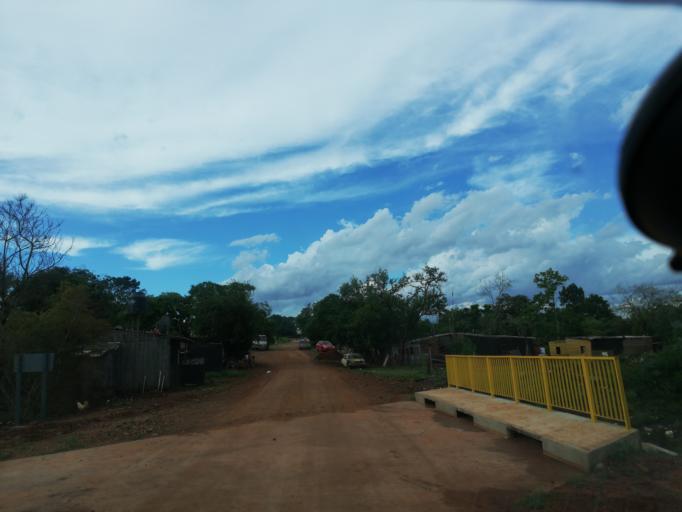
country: AR
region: Misiones
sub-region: Departamento de Capital
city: Posadas
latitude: -27.4222
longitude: -55.9225
